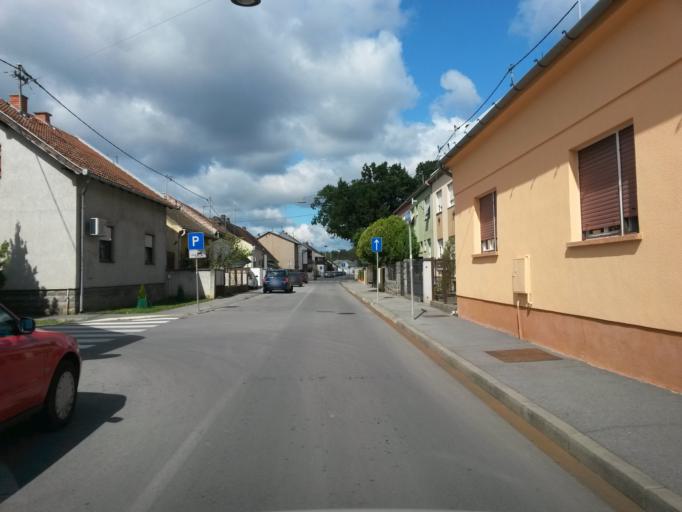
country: HR
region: Osjecko-Baranjska
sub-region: Grad Osijek
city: Osijek
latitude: 45.5612
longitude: 18.6586
